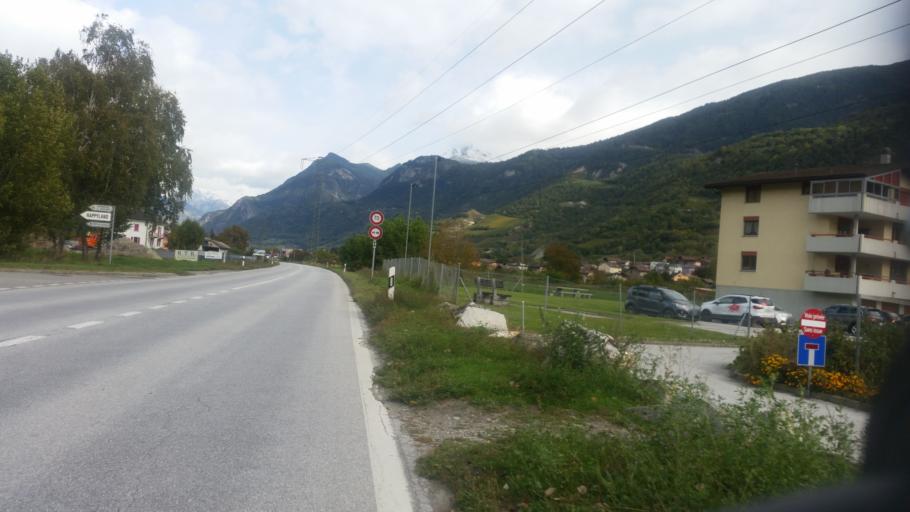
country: CH
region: Valais
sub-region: Sierre District
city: Grone
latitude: 46.2552
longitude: 7.4603
